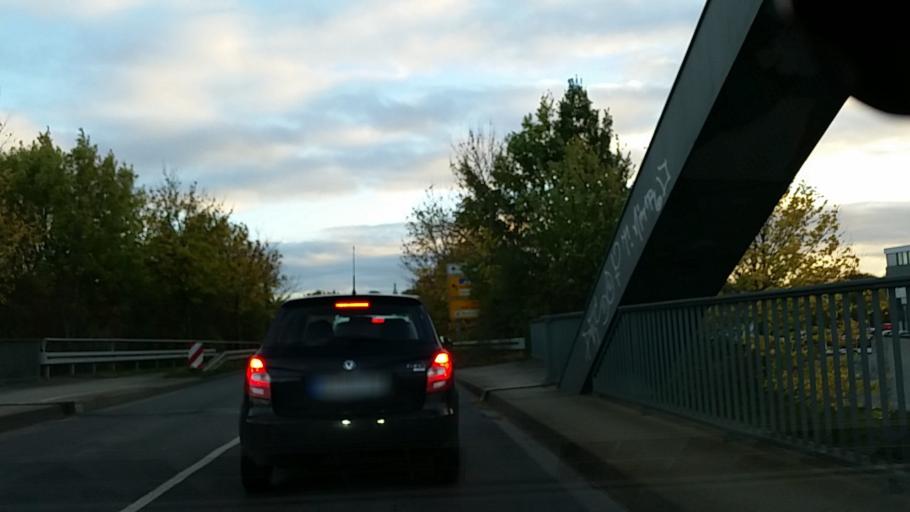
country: DE
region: Lower Saxony
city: Weyhausen
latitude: 52.4256
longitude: 10.7161
